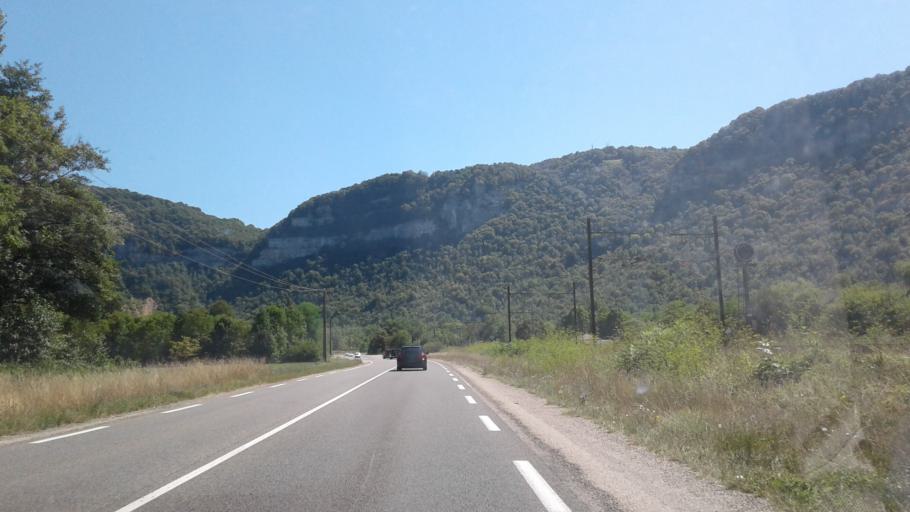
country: FR
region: Rhone-Alpes
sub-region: Departement de l'Ain
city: Vaux-en-Bugey
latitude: 45.9230
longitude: 5.3914
